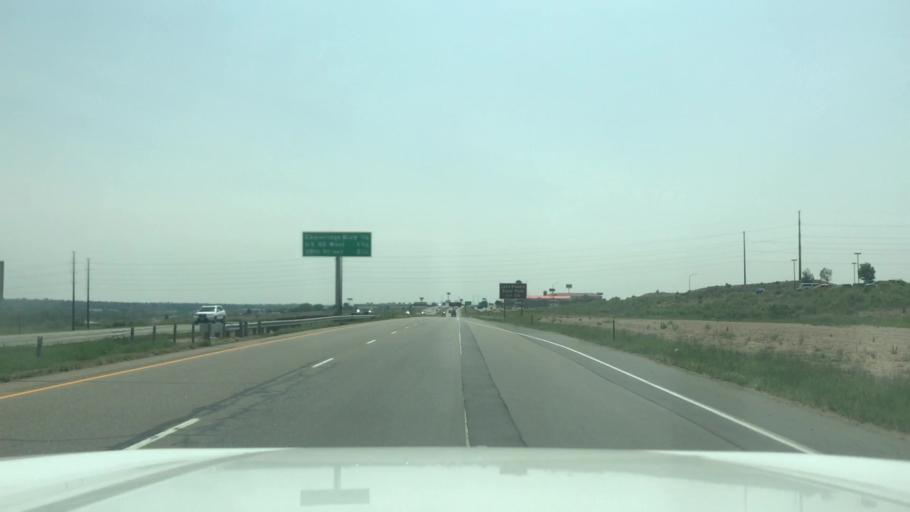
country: US
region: Colorado
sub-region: Pueblo County
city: Pueblo
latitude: 38.3337
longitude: -104.6186
